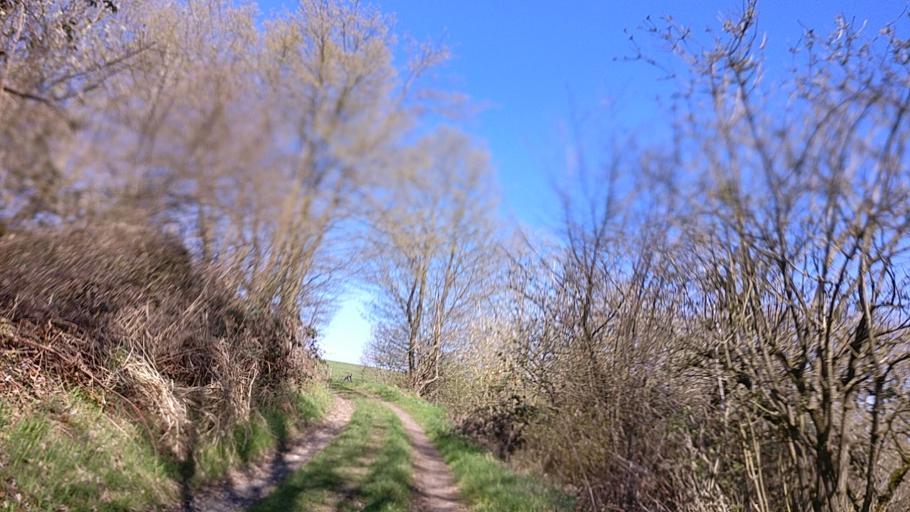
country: DE
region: Rheinland-Pfalz
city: Peterslahr
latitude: 50.6274
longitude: 7.4607
